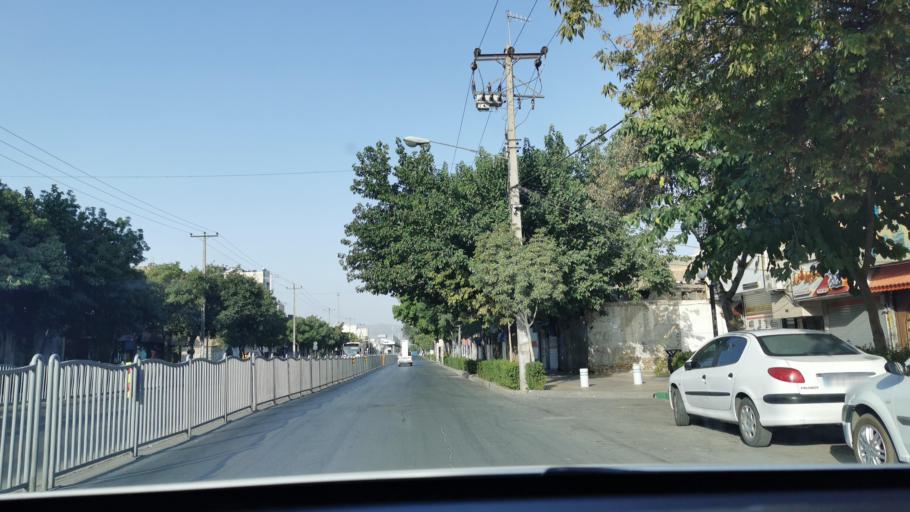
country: IR
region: Razavi Khorasan
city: Mashhad
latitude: 36.3034
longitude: 59.6401
